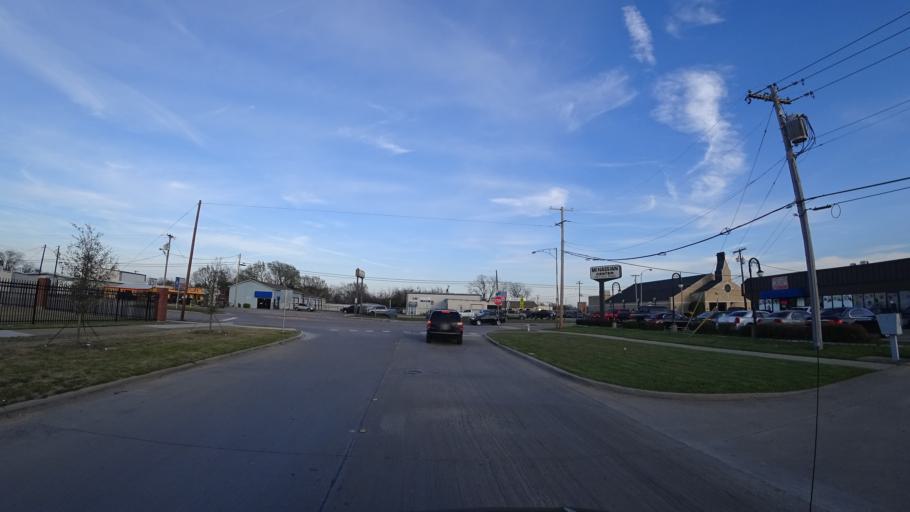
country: US
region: Texas
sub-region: Denton County
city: Lewisville
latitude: 33.0401
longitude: -96.9935
